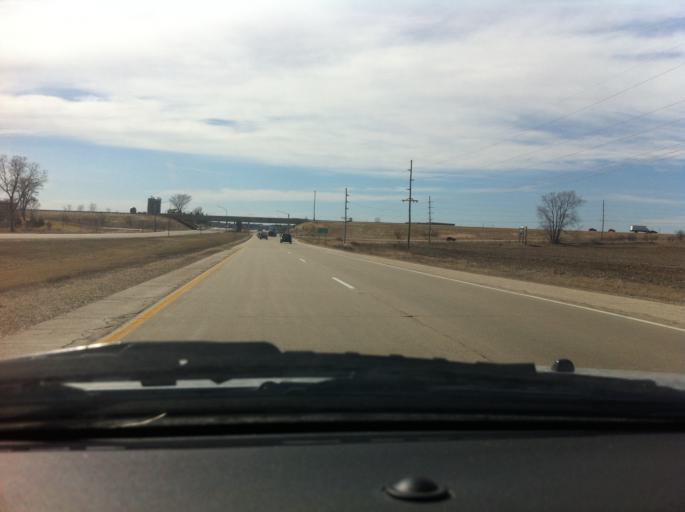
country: US
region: Wisconsin
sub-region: Dane County
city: Windsor
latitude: 43.1949
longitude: -89.3199
